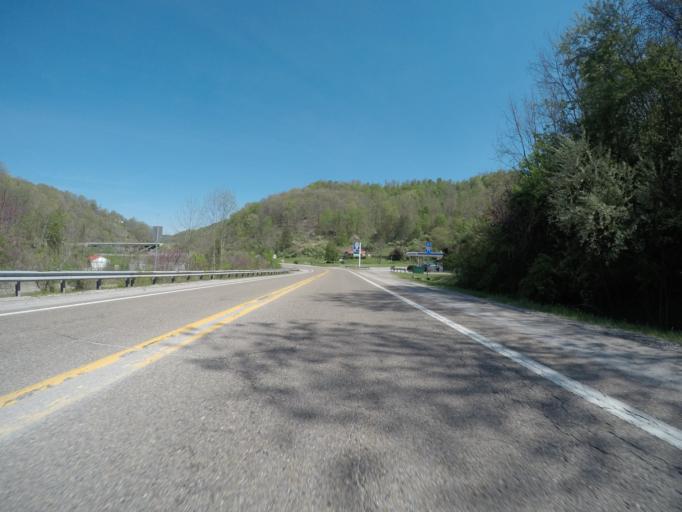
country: US
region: West Virginia
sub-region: Kanawha County
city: Charleston
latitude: 38.4124
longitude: -81.6345
